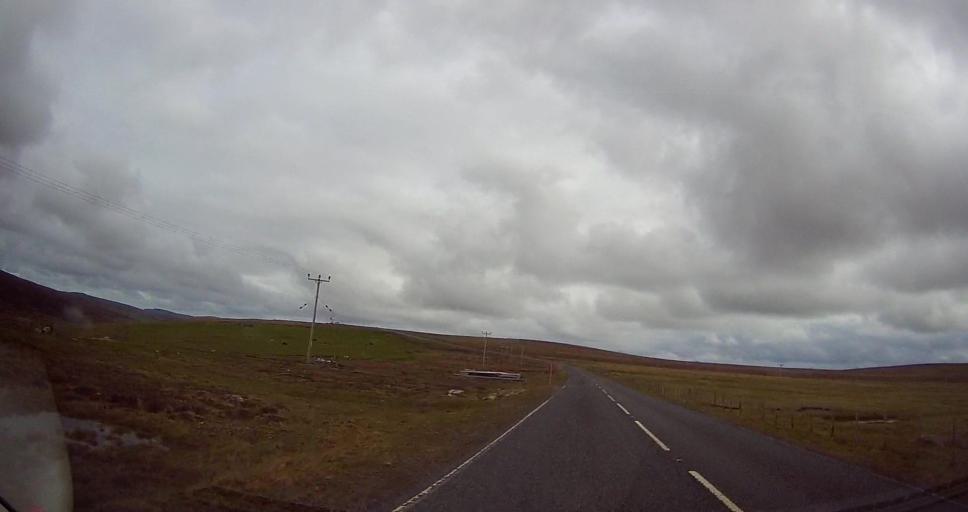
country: GB
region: Scotland
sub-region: Shetland Islands
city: Shetland
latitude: 60.7287
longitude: -0.8999
